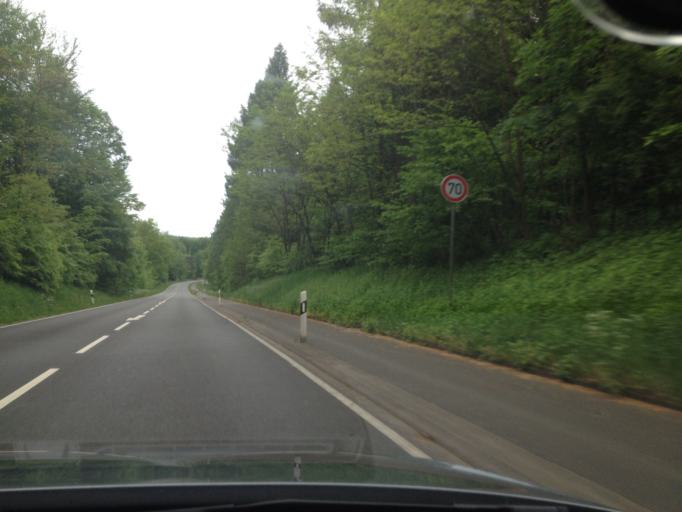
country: DE
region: Saarland
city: Kirkel
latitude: 49.2907
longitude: 7.2167
